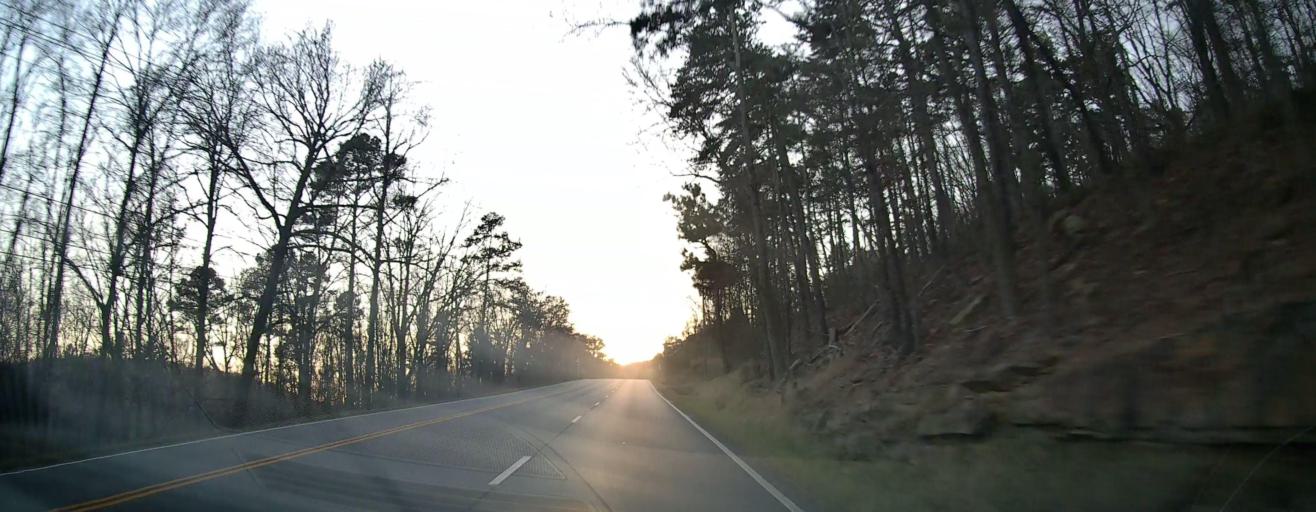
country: US
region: Alabama
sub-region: Etowah County
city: Attalla
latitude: 34.0508
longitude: -86.1681
